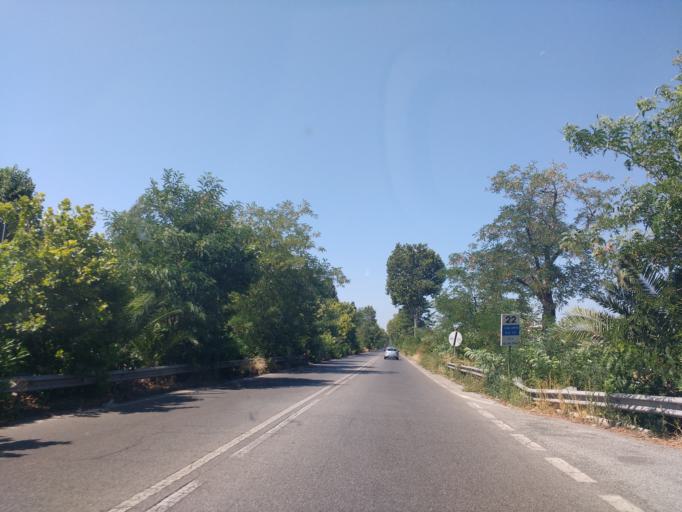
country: IT
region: Latium
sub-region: Citta metropolitana di Roma Capitale
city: Acilia-Castel Fusano-Ostia Antica
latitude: 41.7676
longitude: 12.3188
